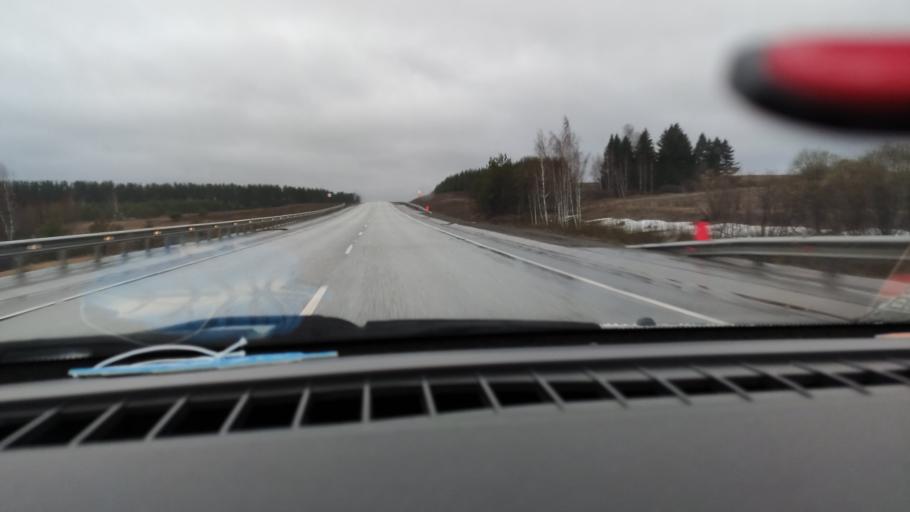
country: RU
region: Udmurtiya
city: Alnashi
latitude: 56.0555
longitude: 52.3928
